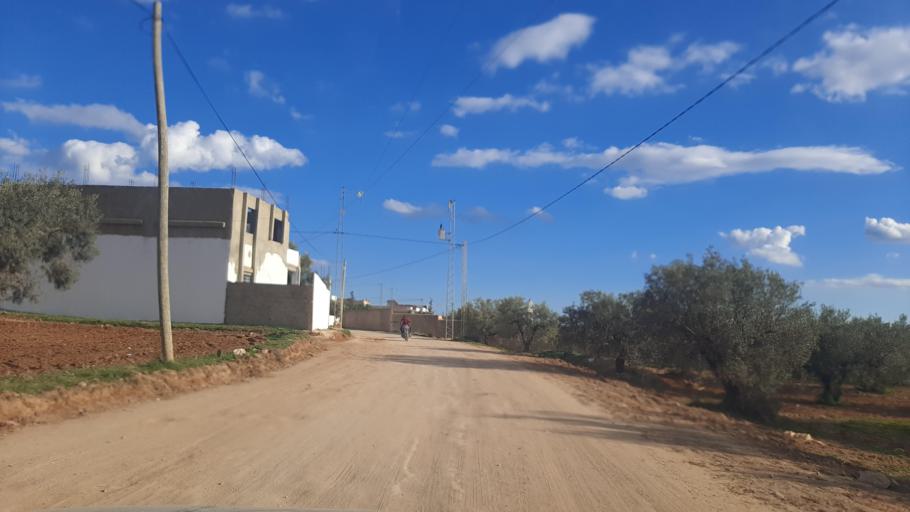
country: TN
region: Nabul
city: Al Hammamat
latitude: 36.4195
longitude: 10.5122
